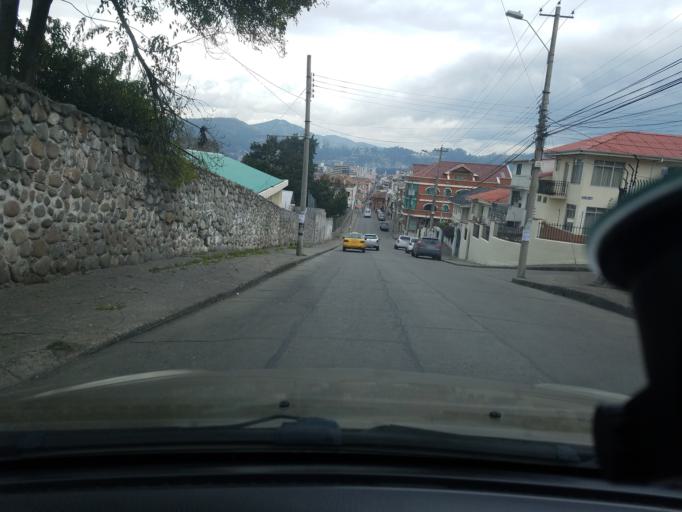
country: EC
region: Azuay
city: Cuenca
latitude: -2.8891
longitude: -79.0015
